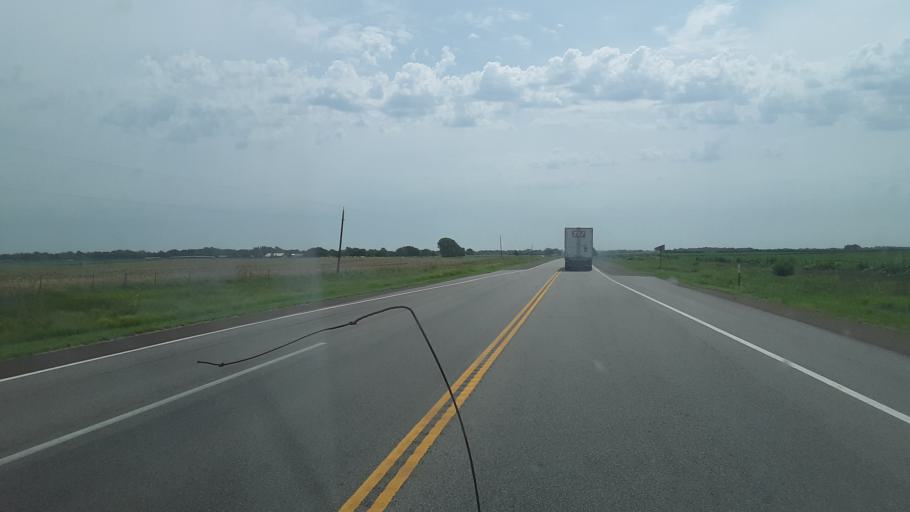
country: US
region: Kansas
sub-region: Reno County
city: South Hutchinson
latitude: 37.9846
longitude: -98.0829
